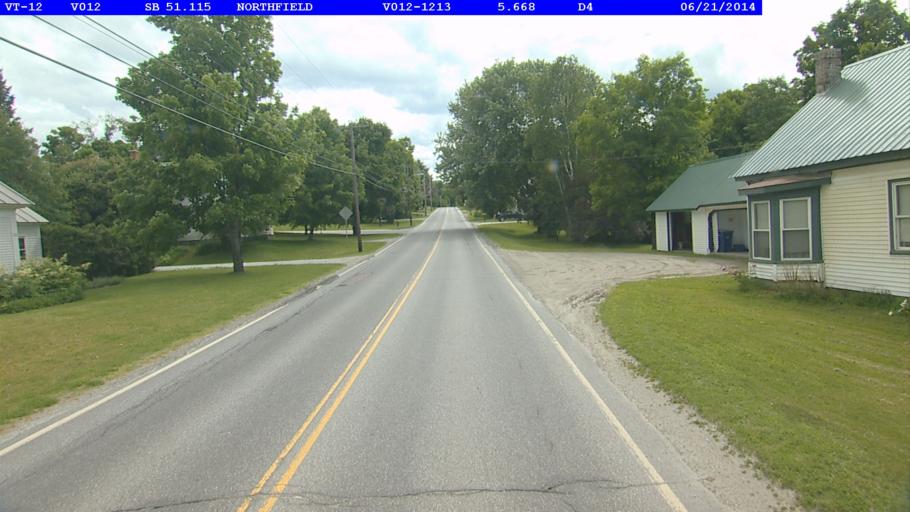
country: US
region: Vermont
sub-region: Washington County
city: Northfield
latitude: 44.1693
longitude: -72.6525
